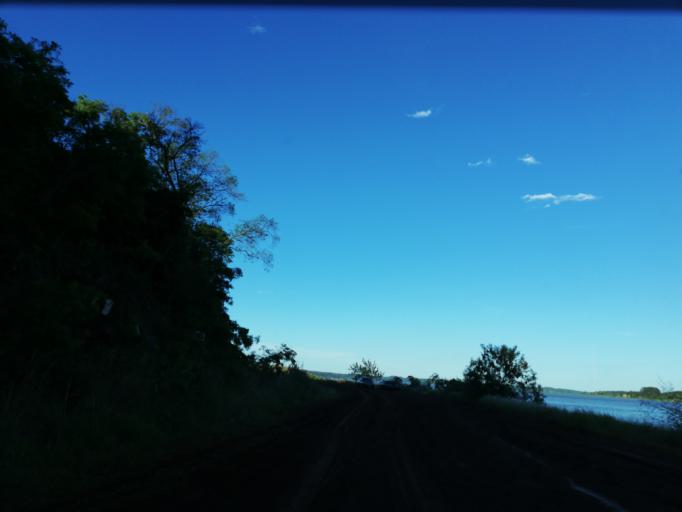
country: AR
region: Misiones
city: Garupa
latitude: -27.4600
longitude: -55.8139
